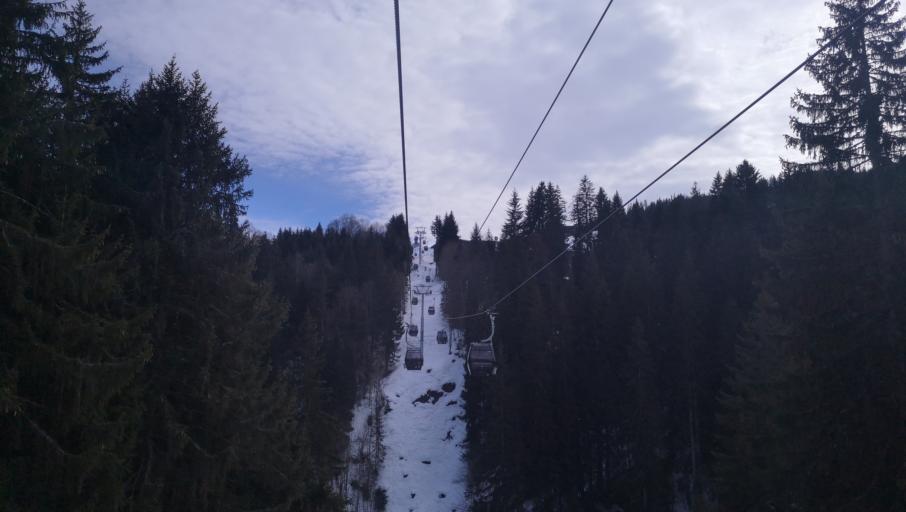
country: FR
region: Rhone-Alpes
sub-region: Departement de la Haute-Savoie
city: Megeve
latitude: 45.8524
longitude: 6.6204
